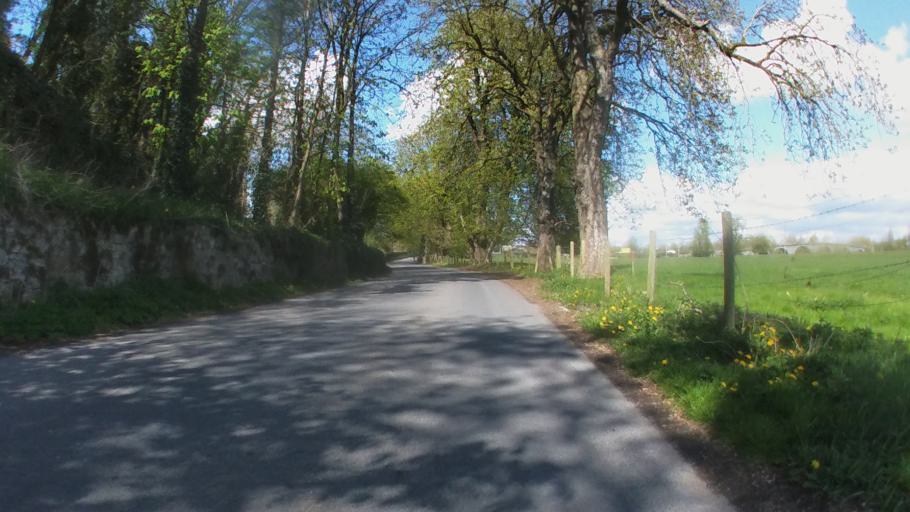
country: IE
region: Leinster
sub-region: Kilkenny
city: Thomastown
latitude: 52.5900
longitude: -7.1868
